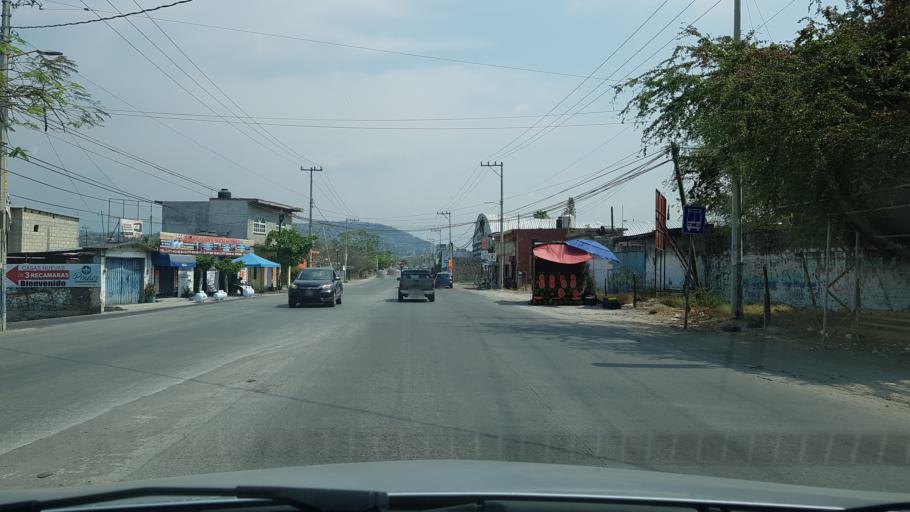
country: MX
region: Morelos
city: Emiliano Zapata
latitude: 18.8236
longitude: -99.1893
